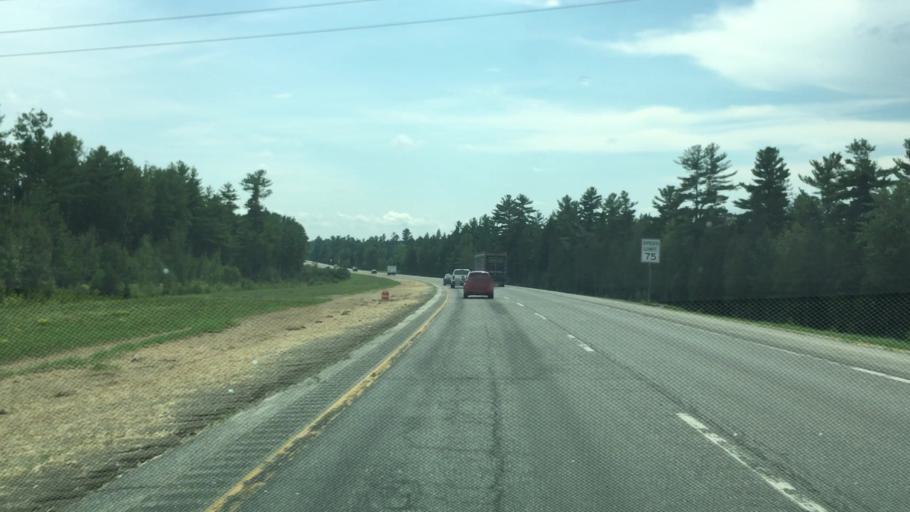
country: US
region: Maine
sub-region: Penobscot County
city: Medway
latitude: 45.5912
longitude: -68.5418
